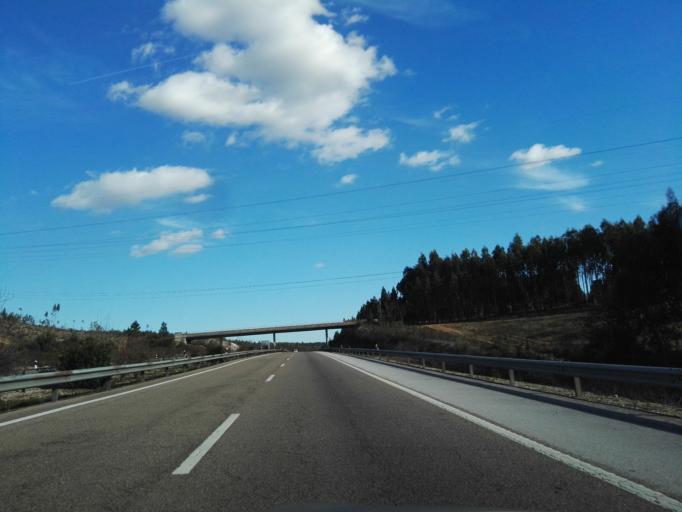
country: PT
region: Santarem
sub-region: Chamusca
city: Vila Nova da Barquinha
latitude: 39.4902
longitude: -8.4340
